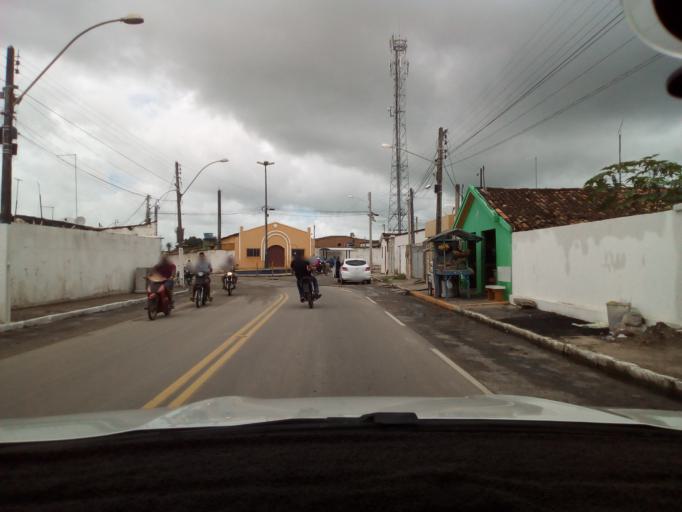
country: BR
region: Paraiba
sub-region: Pedras De Fogo
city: Pedras de Fogo
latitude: -7.4049
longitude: -35.1106
